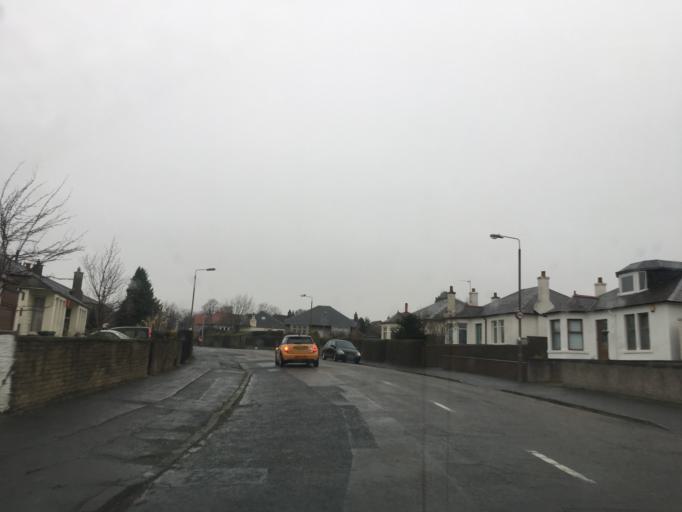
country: GB
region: Scotland
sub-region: Edinburgh
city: Colinton
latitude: 55.9469
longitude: -3.2891
